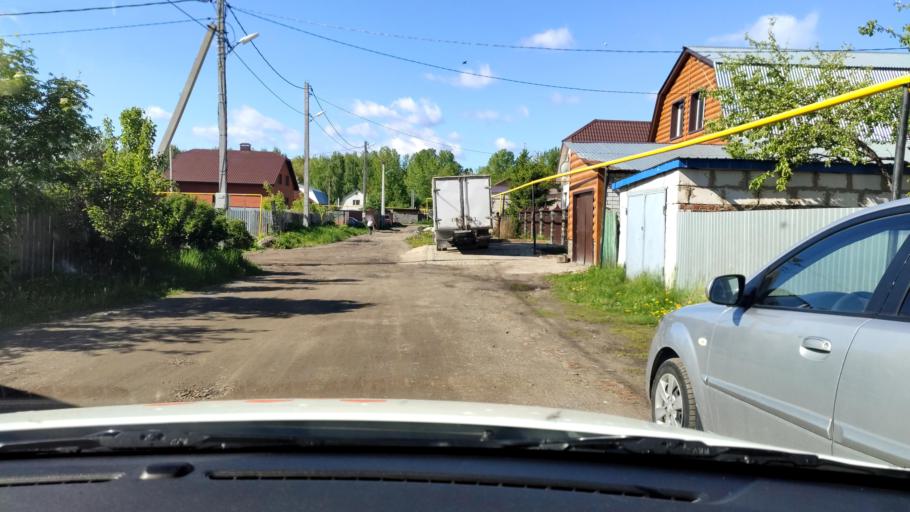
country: RU
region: Tatarstan
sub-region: Gorod Kazan'
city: Kazan
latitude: 55.7361
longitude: 49.0903
